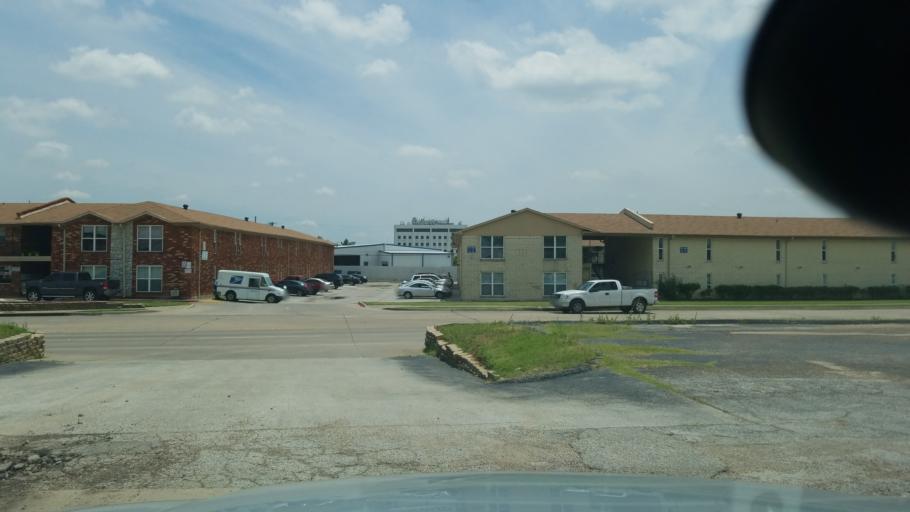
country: US
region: Texas
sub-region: Dallas County
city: Irving
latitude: 32.8422
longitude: -96.9745
